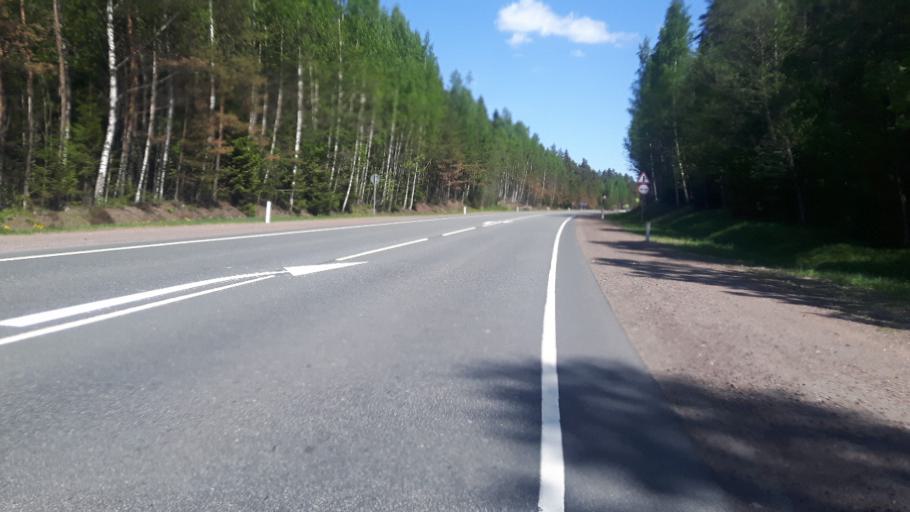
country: RU
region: Leningrad
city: Vysotsk
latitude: 60.6353
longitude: 28.2775
